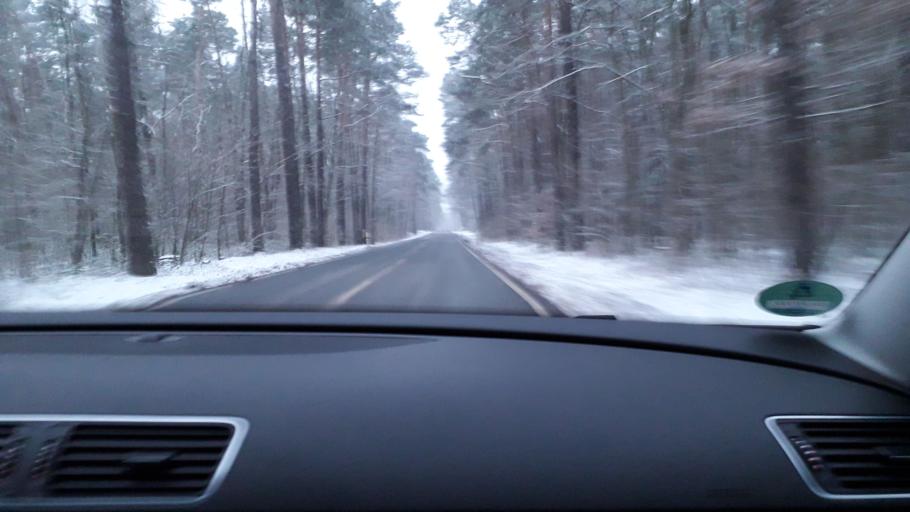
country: DE
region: Brandenburg
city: Spremberg
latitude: 51.5915
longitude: 14.4341
